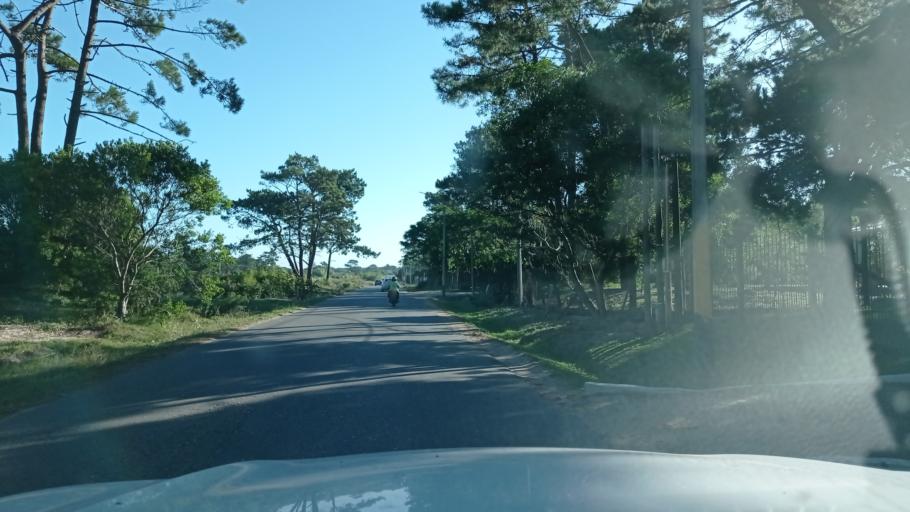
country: UY
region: Canelones
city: Pando
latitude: -34.8084
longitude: -55.9125
